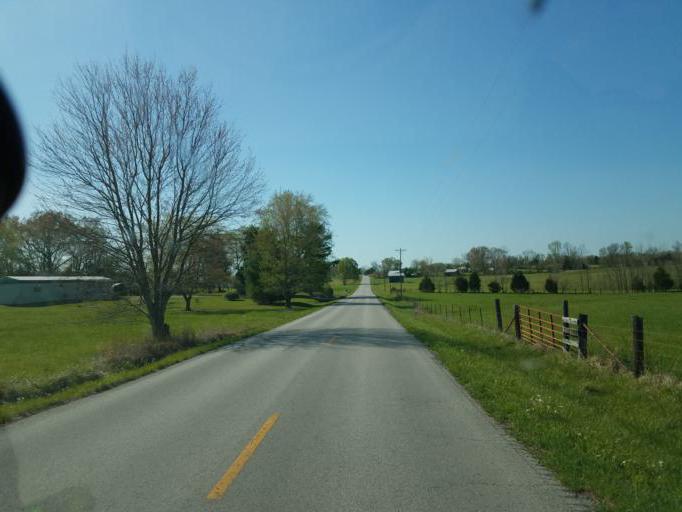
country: US
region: Kentucky
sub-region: Edmonson County
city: Brownsville
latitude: 37.1272
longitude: -86.1606
